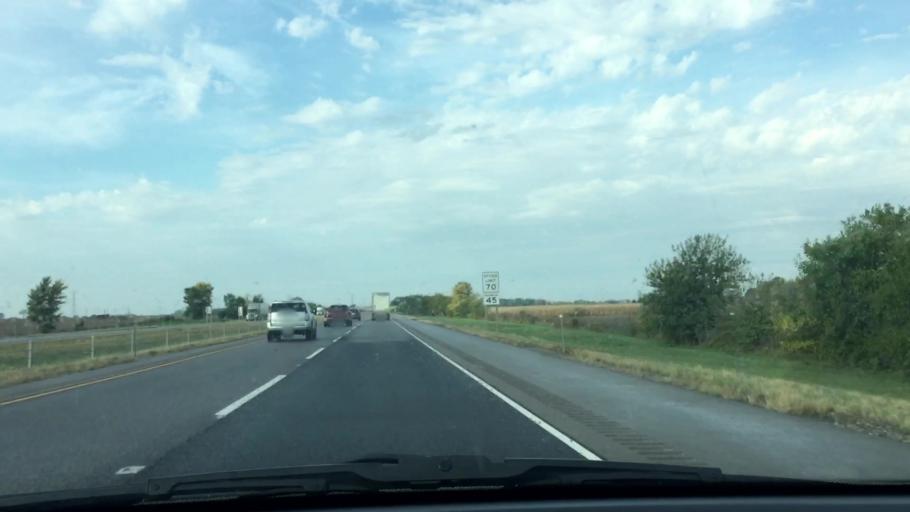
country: US
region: Illinois
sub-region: Lee County
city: Dixon
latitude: 41.7771
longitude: -89.5708
